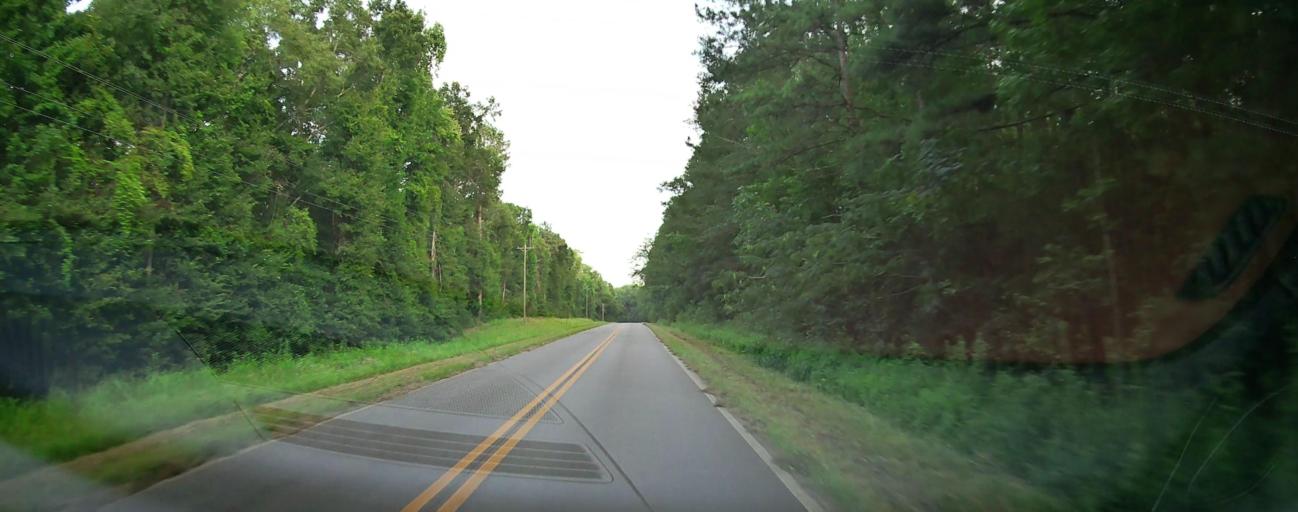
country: US
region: Georgia
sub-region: Crawford County
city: Roberta
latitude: 32.6756
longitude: -84.0833
